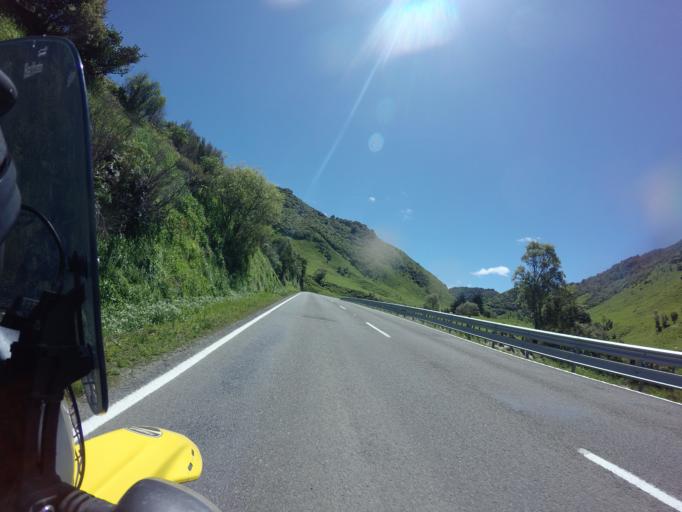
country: NZ
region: Bay of Plenty
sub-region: Opotiki District
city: Opotiki
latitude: -38.3676
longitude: 177.4634
